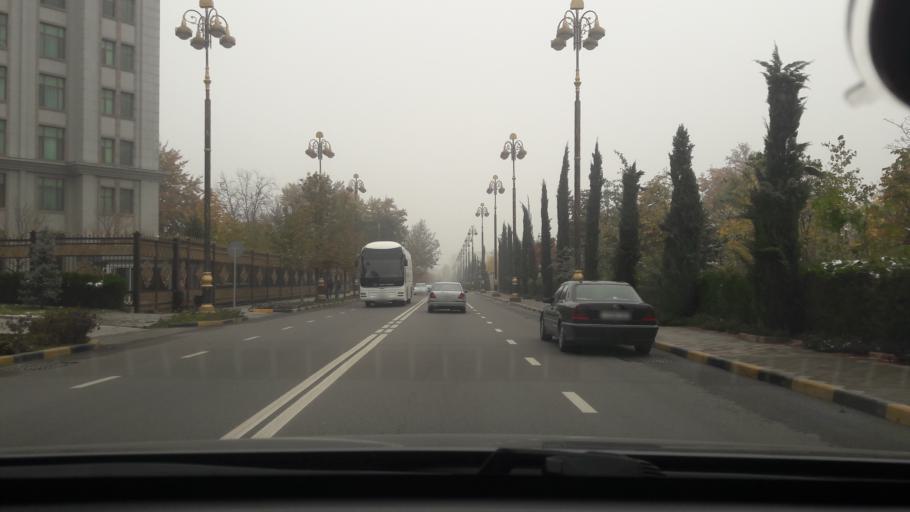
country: TJ
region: Dushanbe
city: Dushanbe
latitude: 38.5793
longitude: 68.7822
